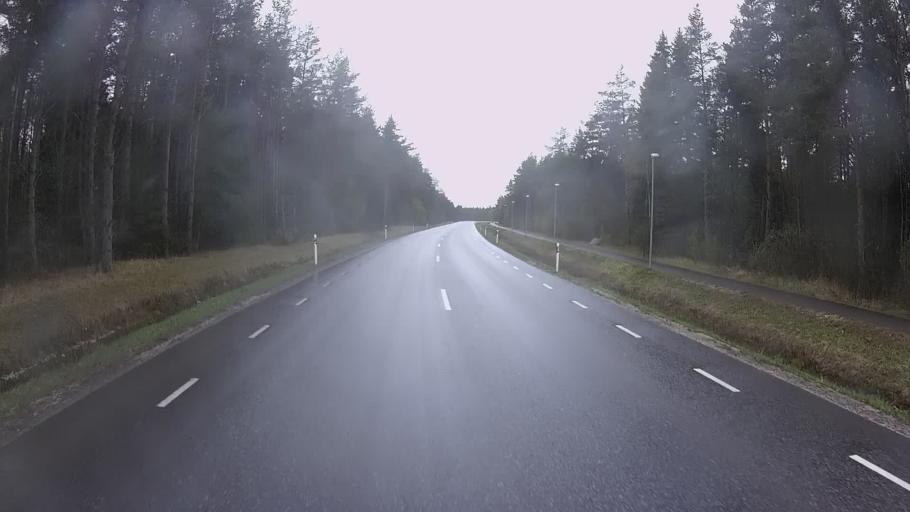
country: EE
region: Hiiumaa
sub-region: Kaerdla linn
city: Kardla
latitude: 58.9796
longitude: 22.5079
